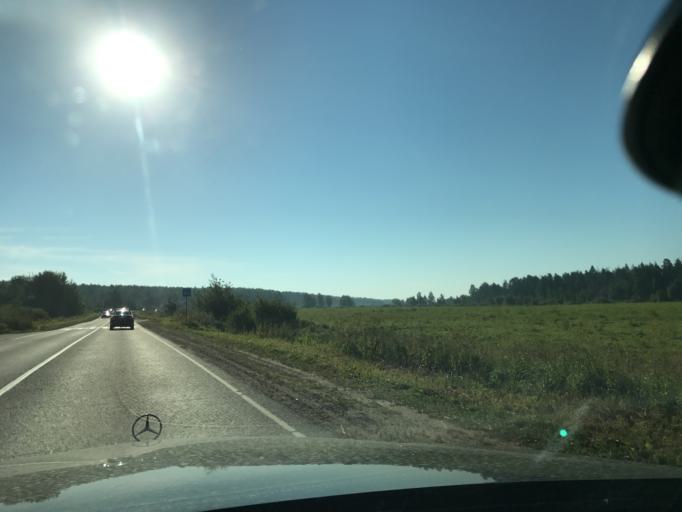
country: RU
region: Moskovskaya
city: Bakhchivandzhi
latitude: 55.8608
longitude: 38.0528
